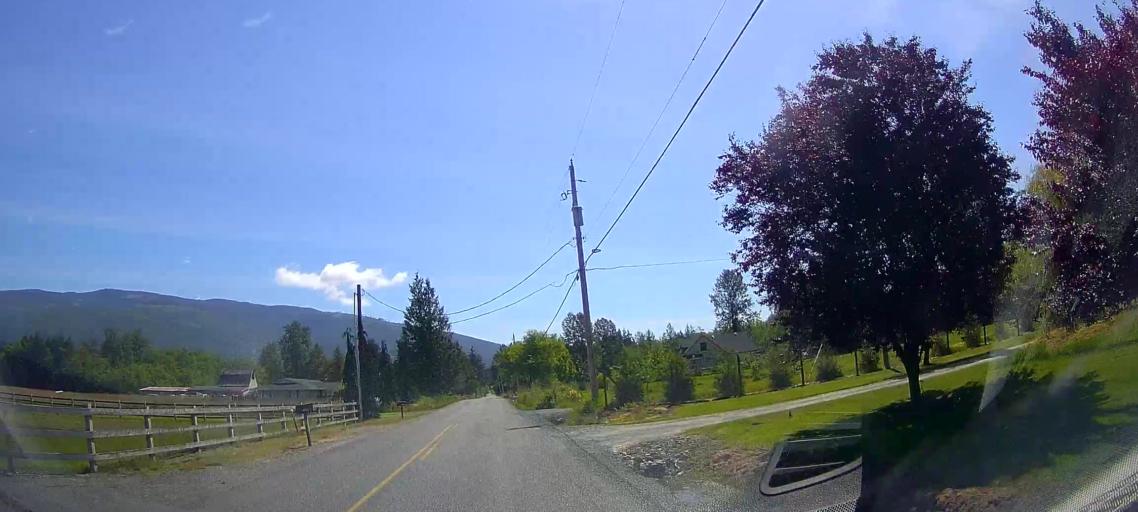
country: US
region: Washington
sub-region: Skagit County
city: Sedro-Woolley
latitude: 48.5579
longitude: -122.2554
